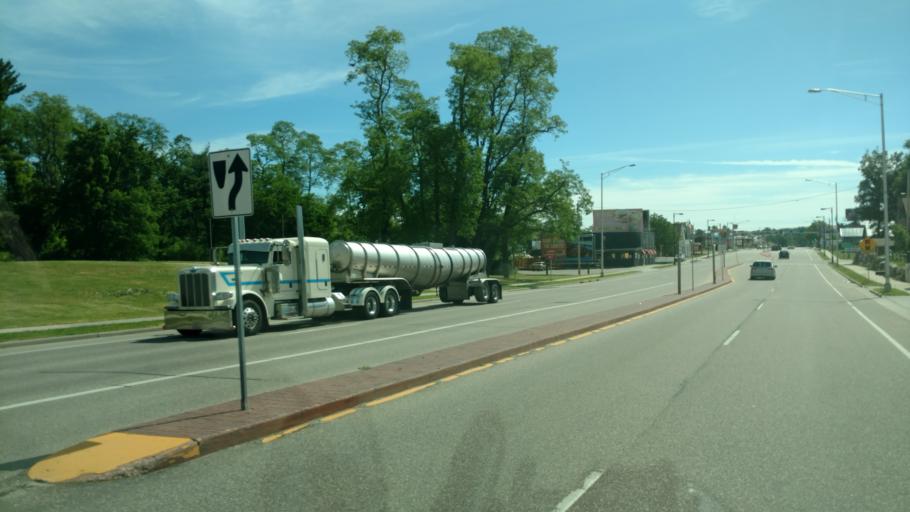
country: US
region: Wisconsin
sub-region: Sauk County
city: Lake Delton
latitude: 43.5891
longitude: -89.7975
